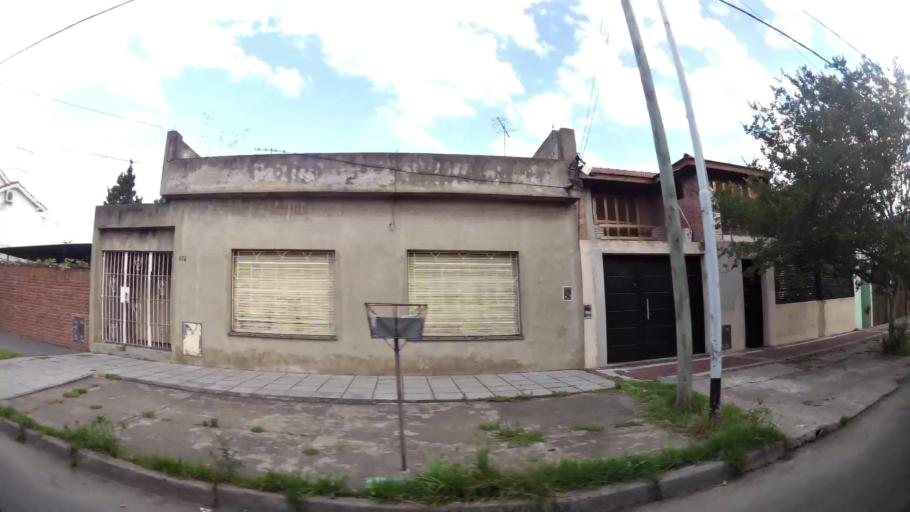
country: AR
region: Buenos Aires
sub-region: Partido de Avellaneda
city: Avellaneda
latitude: -34.6761
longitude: -58.3598
